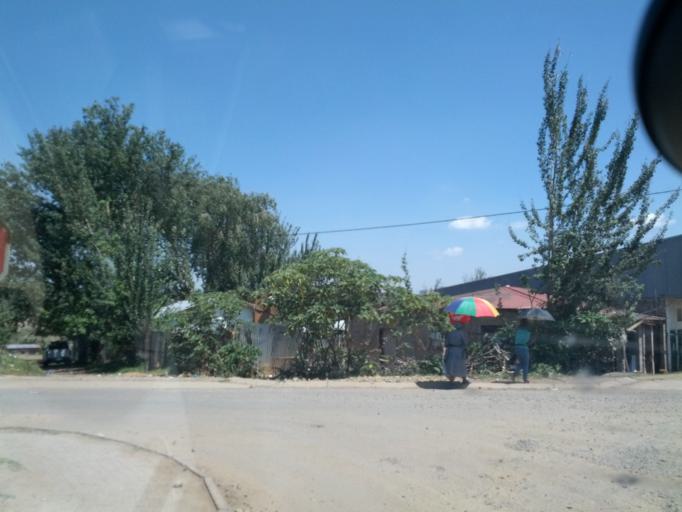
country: LS
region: Butha-Buthe
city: Butha-Buthe
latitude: -28.7621
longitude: 28.2477
